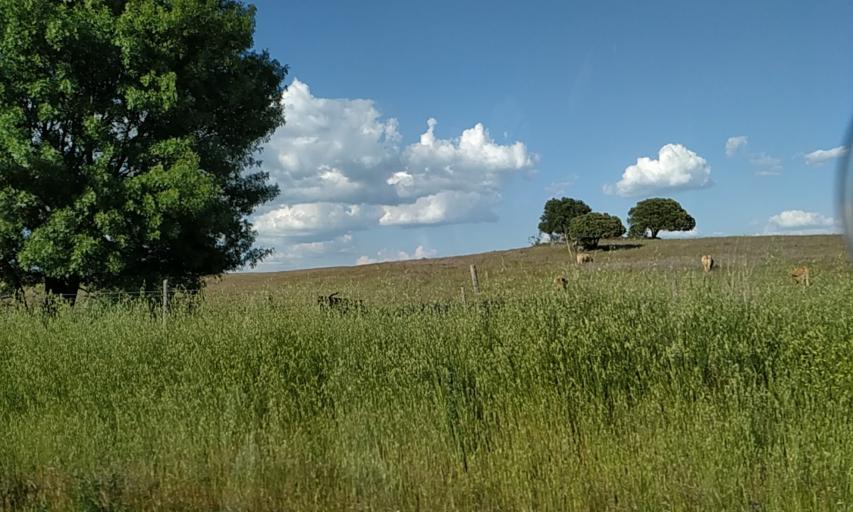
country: PT
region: Portalegre
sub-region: Portalegre
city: Urra
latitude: 39.1211
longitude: -7.4430
